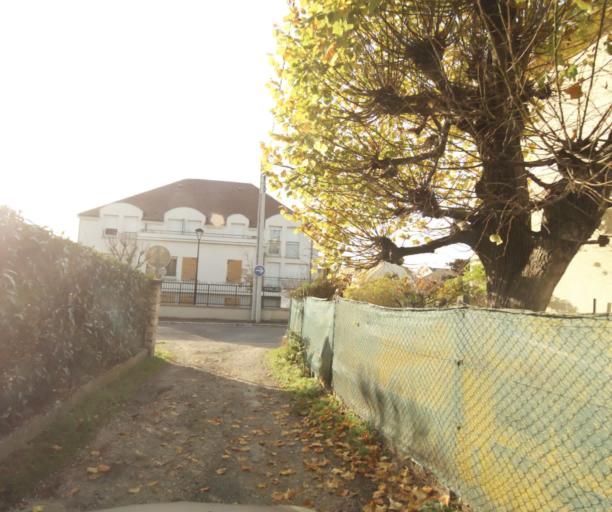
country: FR
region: Ile-de-France
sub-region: Departement des Yvelines
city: Triel-sur-Seine
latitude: 48.9761
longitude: 2.0037
